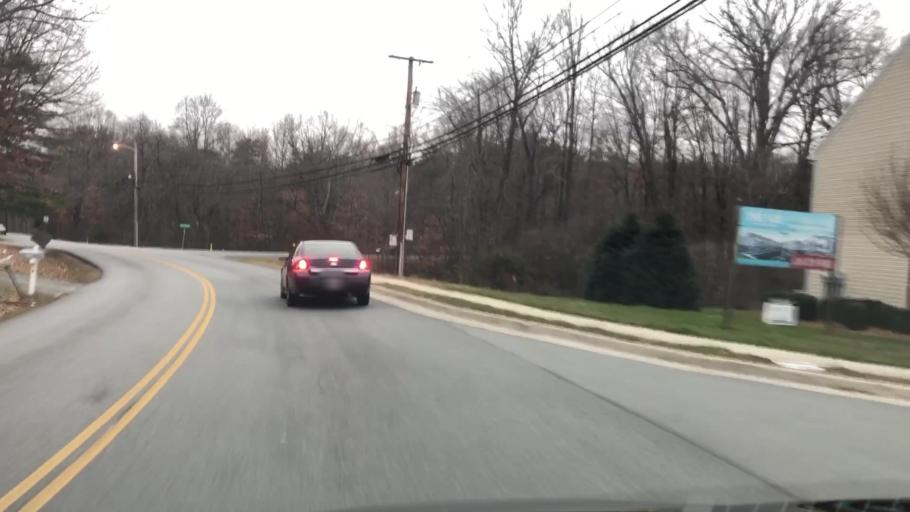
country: US
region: Virginia
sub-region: City of Lynchburg
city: West Lynchburg
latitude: 37.3553
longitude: -79.1884
